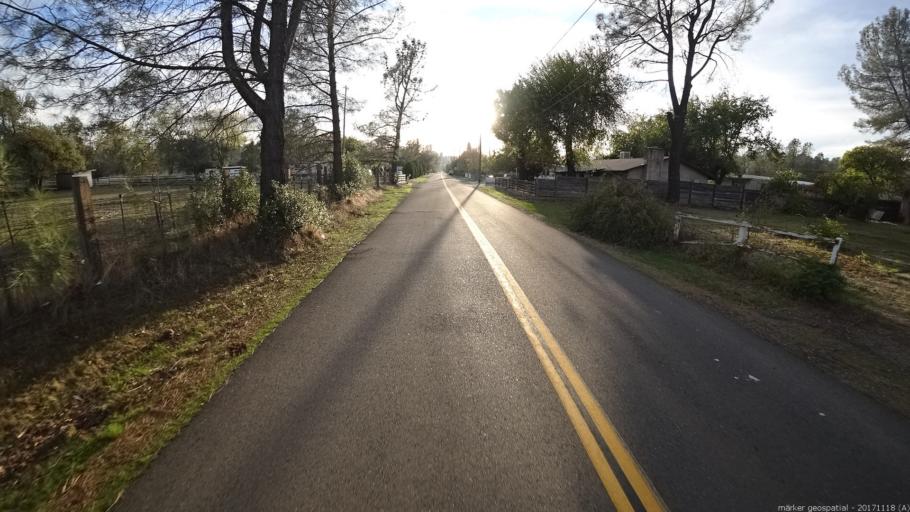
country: US
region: California
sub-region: Shasta County
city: Anderson
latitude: 40.4623
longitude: -122.3311
